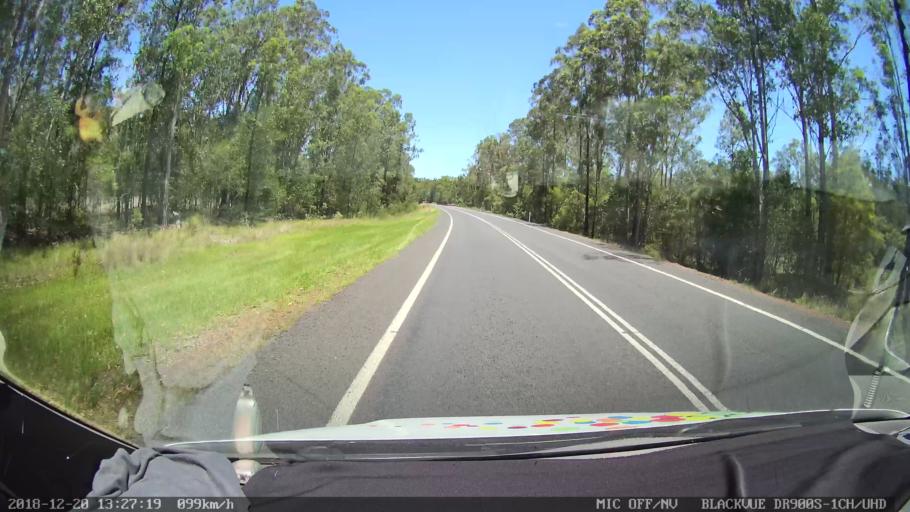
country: AU
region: New South Wales
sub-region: Richmond Valley
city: Casino
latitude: -29.1583
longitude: 152.9919
